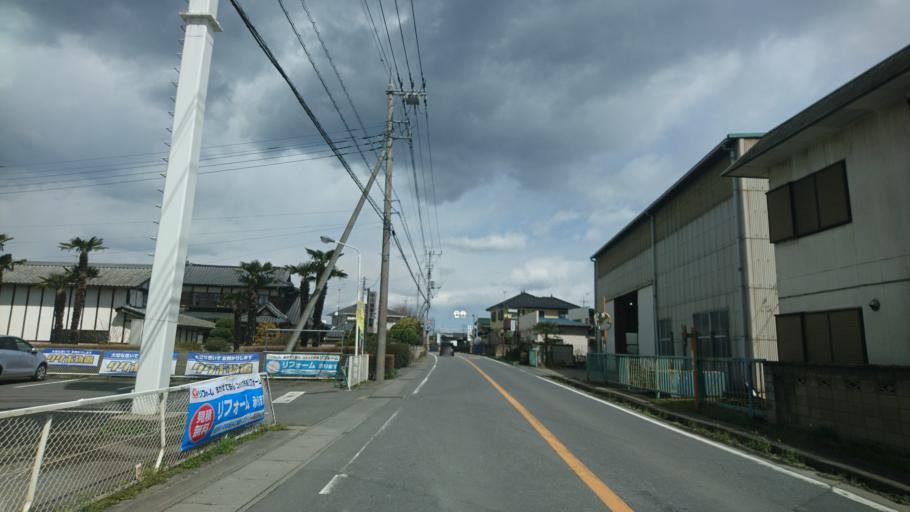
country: JP
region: Ibaraki
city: Yuki
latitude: 36.2597
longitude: 139.9142
